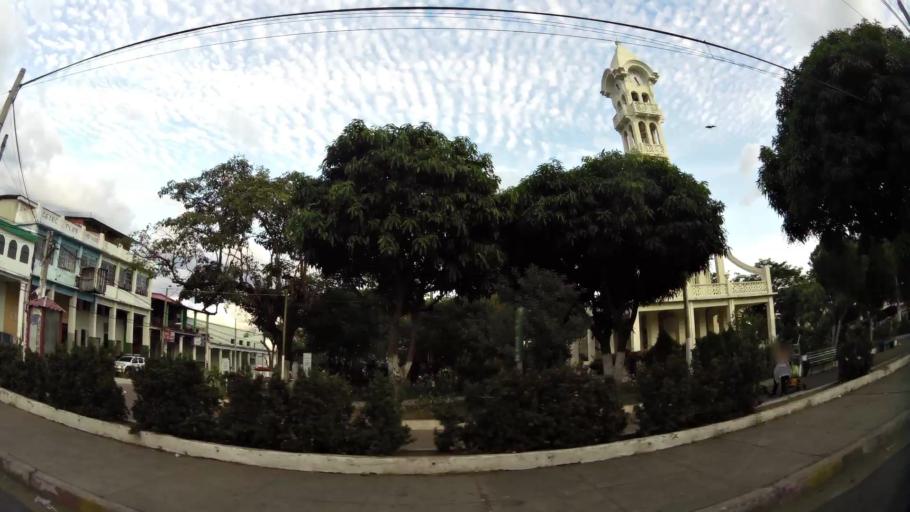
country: SV
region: San Vicente
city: San Vicente
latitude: 13.6455
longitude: -88.7845
